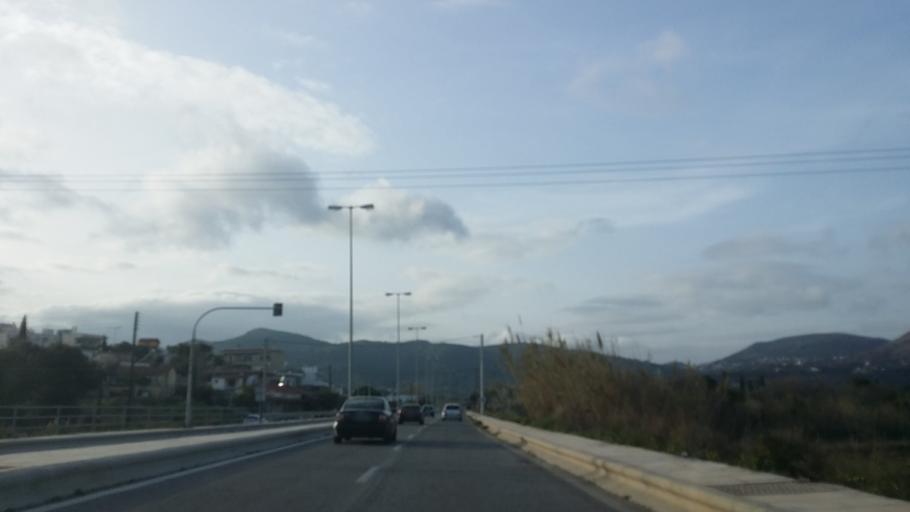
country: GR
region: Attica
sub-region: Nomarchia Anatolikis Attikis
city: Lavrio
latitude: 37.7323
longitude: 24.0507
